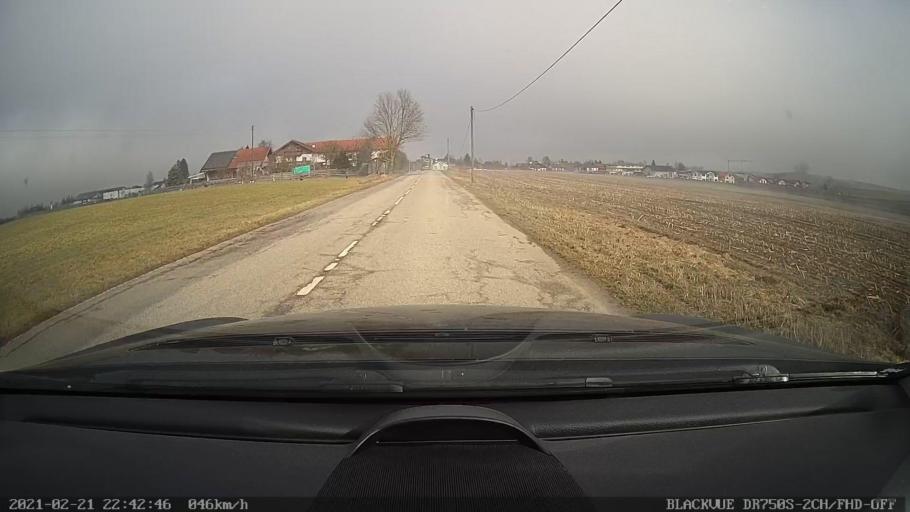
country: DE
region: Bavaria
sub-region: Upper Bavaria
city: Griesstatt
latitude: 47.9856
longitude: 12.1787
